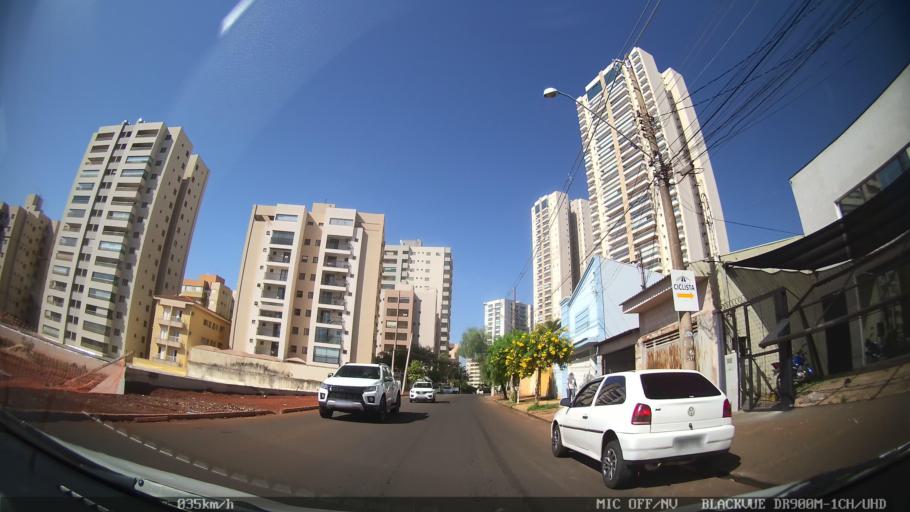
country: BR
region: Sao Paulo
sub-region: Ribeirao Preto
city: Ribeirao Preto
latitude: -21.2071
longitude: -47.7962
